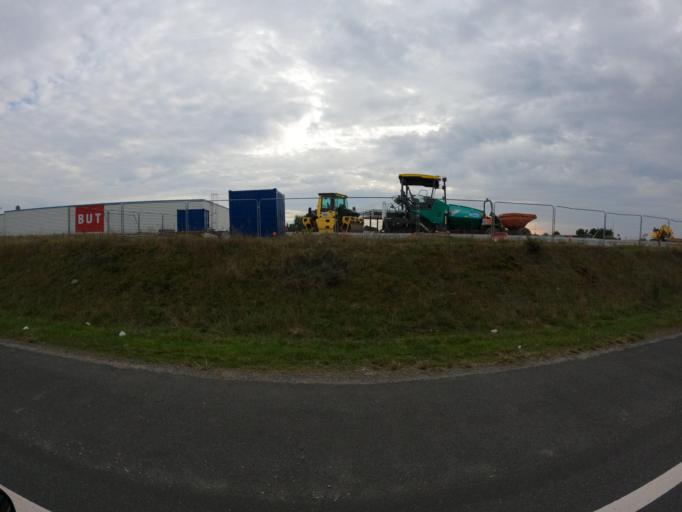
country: FR
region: Pays de la Loire
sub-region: Departement de la Loire-Atlantique
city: Clisson
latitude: 47.0997
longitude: -1.2813
